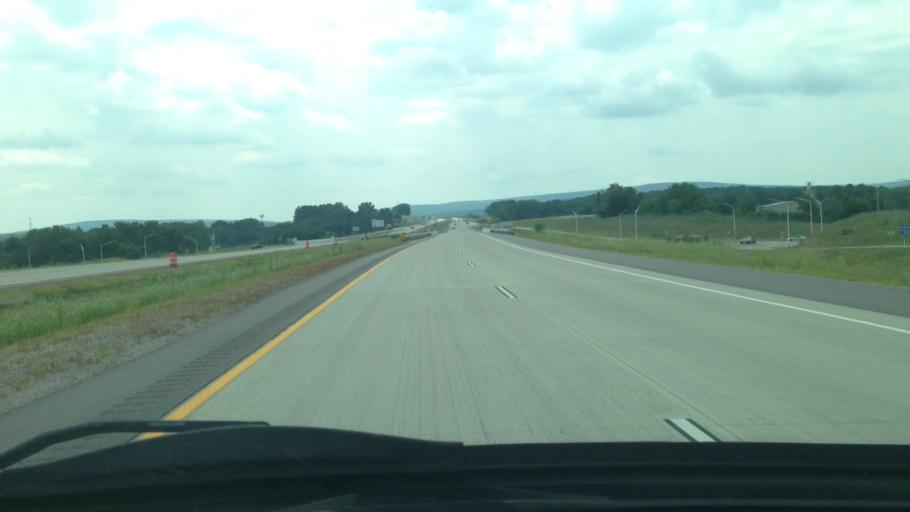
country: US
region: Wisconsin
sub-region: Sauk County
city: West Baraboo
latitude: 43.4769
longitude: -89.7748
